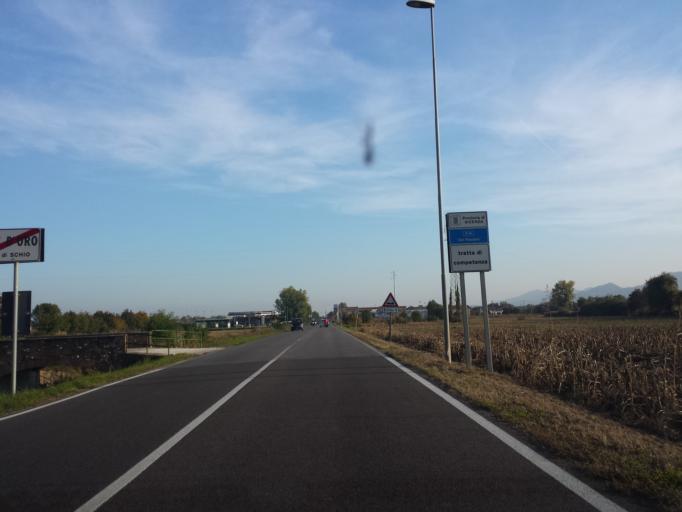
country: IT
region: Veneto
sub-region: Provincia di Vicenza
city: San Vito di Leguzzano
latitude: 45.6961
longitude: 11.3855
